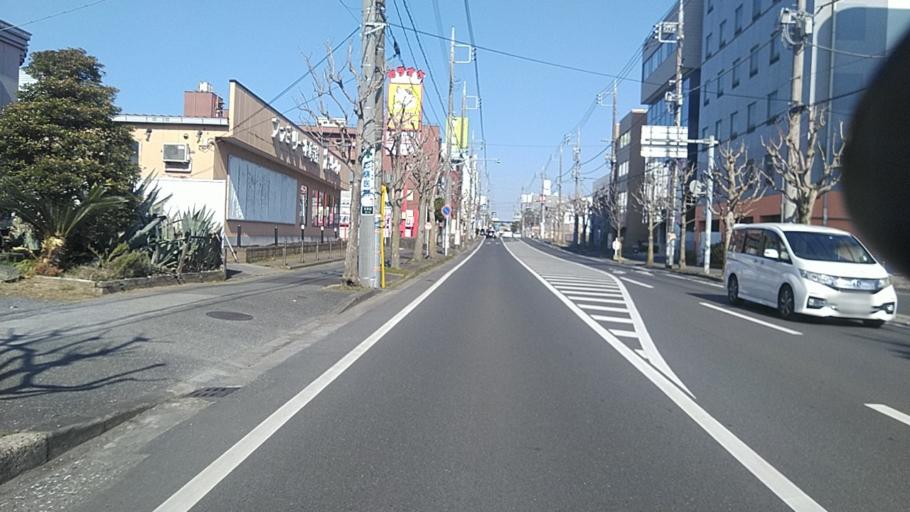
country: JP
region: Chiba
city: Mobara
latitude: 35.4228
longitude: 140.3007
